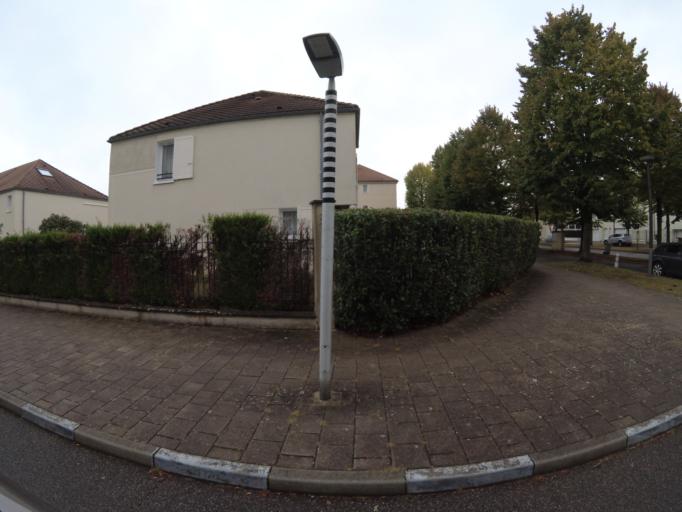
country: FR
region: Ile-de-France
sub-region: Departement de Seine-et-Marne
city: Bussy-Saint-Georges
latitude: 48.8405
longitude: 2.7149
